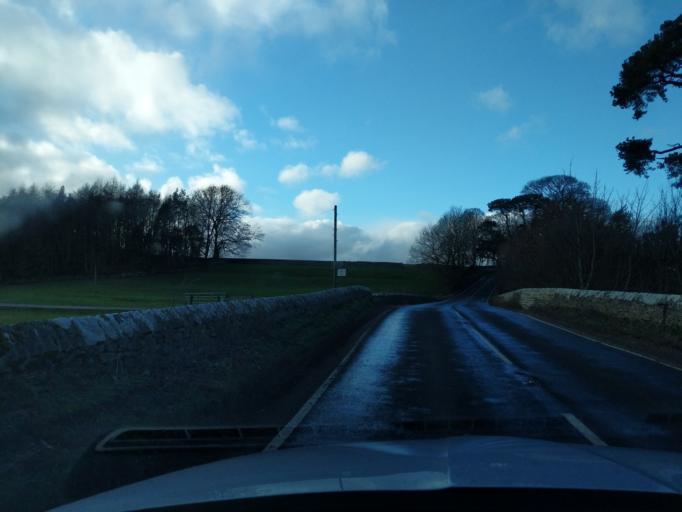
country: GB
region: England
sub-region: North Yorkshire
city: Leyburn
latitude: 54.3546
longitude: -1.8147
